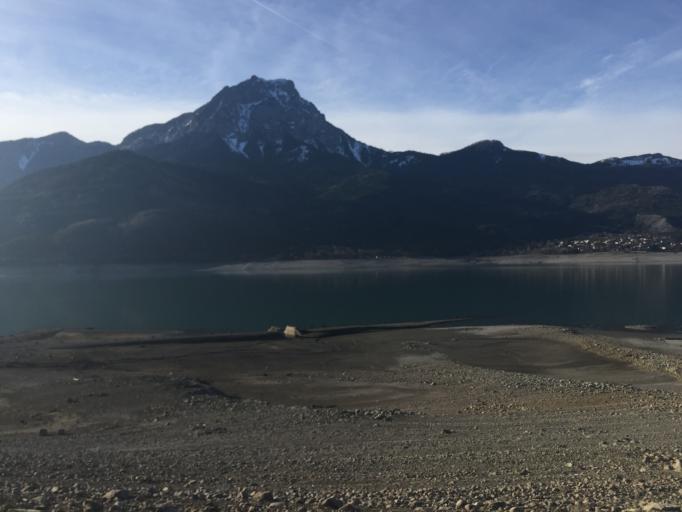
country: FR
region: Provence-Alpes-Cote d'Azur
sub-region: Departement des Hautes-Alpes
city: Chorges
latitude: 44.5354
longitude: 6.3819
